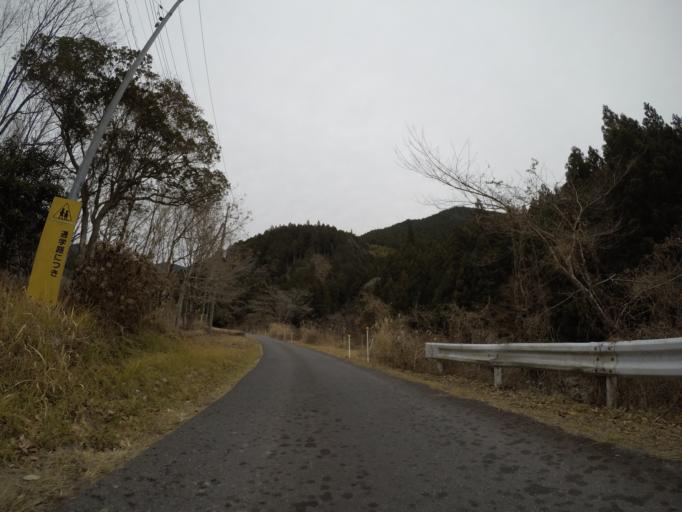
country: JP
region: Shizuoka
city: Fujinomiya
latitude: 35.2704
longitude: 138.5301
